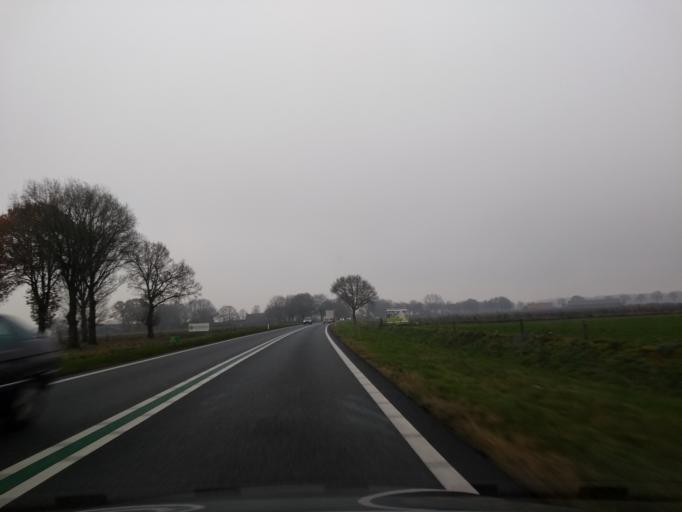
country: NL
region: Overijssel
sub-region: Gemeente Twenterand
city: Vroomshoop
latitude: 52.5248
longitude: 6.5557
